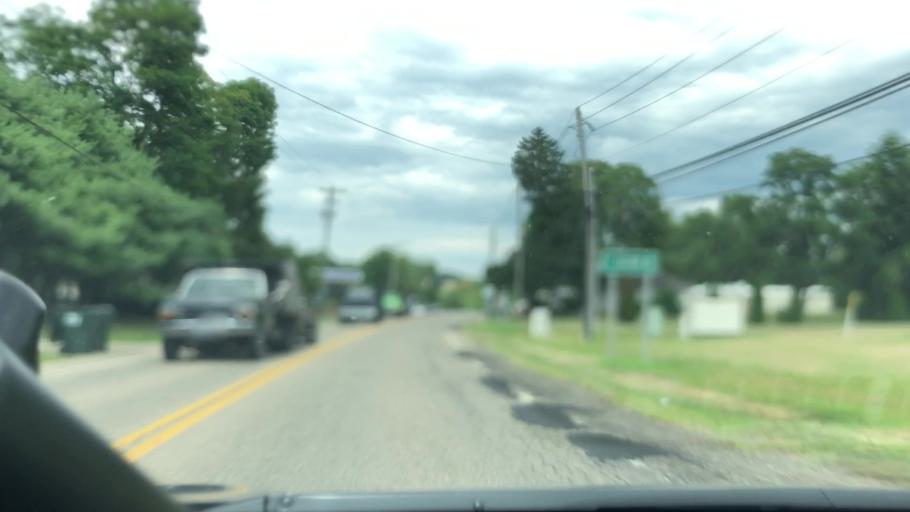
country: US
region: Ohio
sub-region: Summit County
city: New Franklin
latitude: 40.9561
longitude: -81.5319
